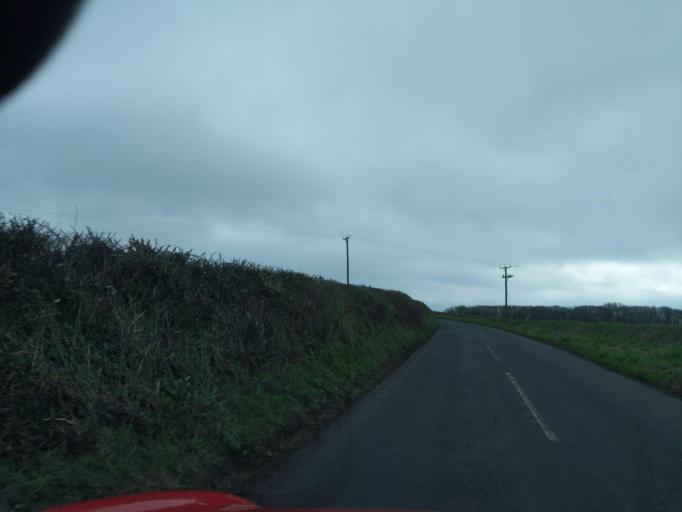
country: GB
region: England
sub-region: Devon
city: Wembury
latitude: 50.3360
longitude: -4.0954
